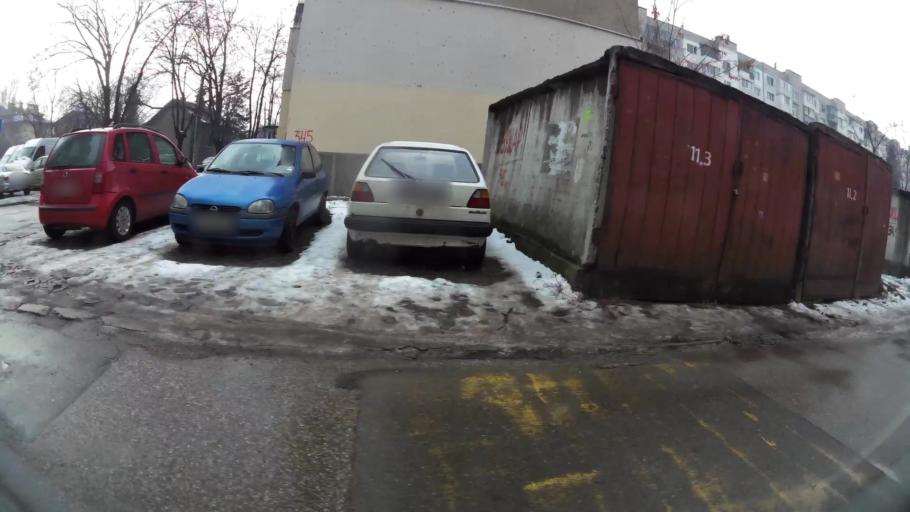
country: BG
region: Sofia-Capital
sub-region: Stolichna Obshtina
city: Sofia
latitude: 42.6946
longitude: 23.2865
